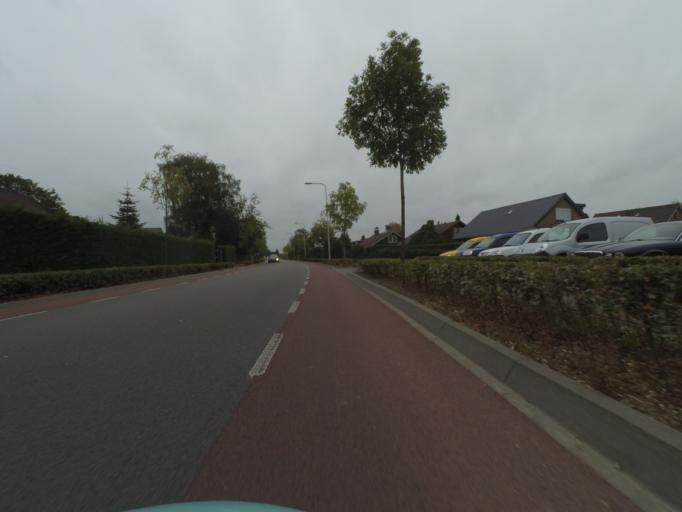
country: NL
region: Gelderland
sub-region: Gemeente Geldermalsen
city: Geldermalsen
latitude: 51.9095
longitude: 5.3391
